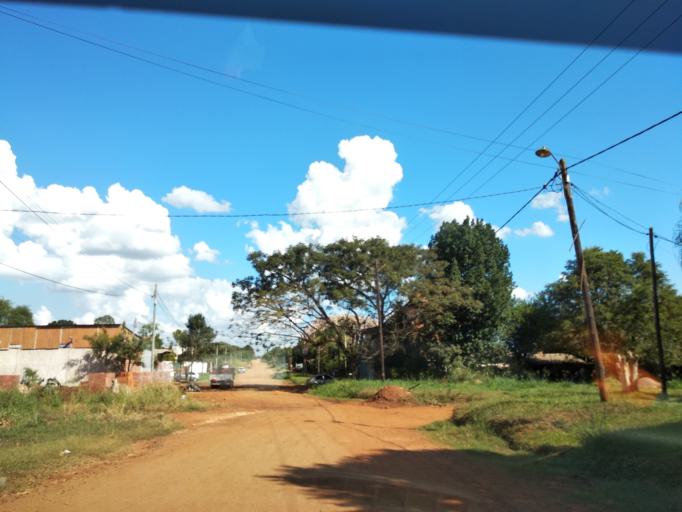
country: AR
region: Misiones
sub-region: Departamento de Capital
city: Posadas
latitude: -27.3775
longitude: -55.9446
